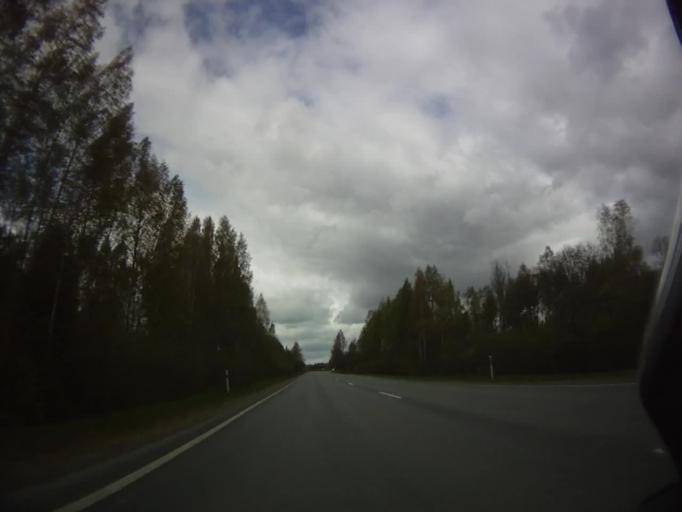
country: LV
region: Pargaujas
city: Stalbe
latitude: 57.3137
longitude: 24.9236
